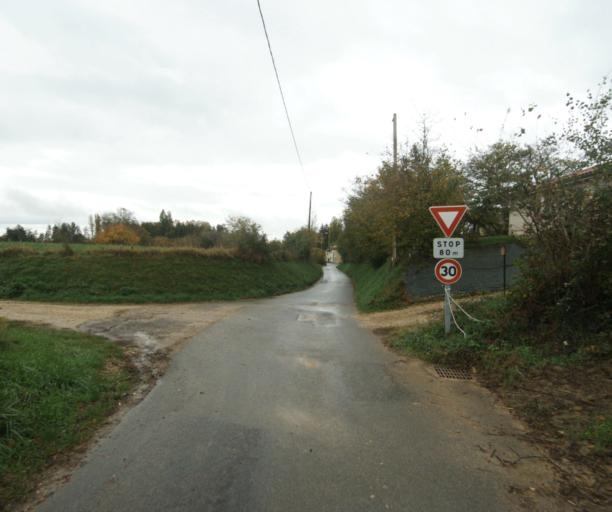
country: FR
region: Rhone-Alpes
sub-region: Departement de l'Ain
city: Pont-de-Vaux
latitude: 46.4836
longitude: 4.8688
